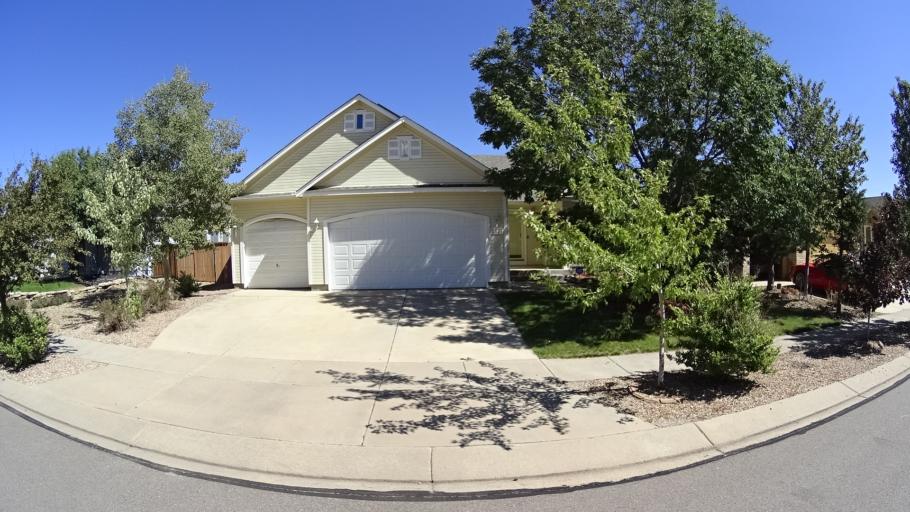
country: US
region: Colorado
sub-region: El Paso County
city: Security-Widefield
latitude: 38.7822
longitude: -104.7272
